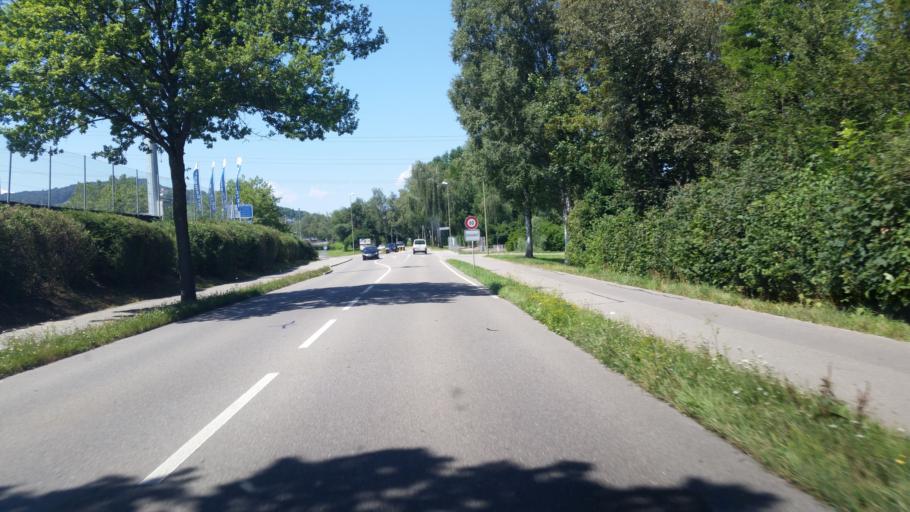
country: CH
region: Zurich
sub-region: Bezirk Dielsdorf
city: Niederhasli
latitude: 47.4830
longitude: 8.4742
